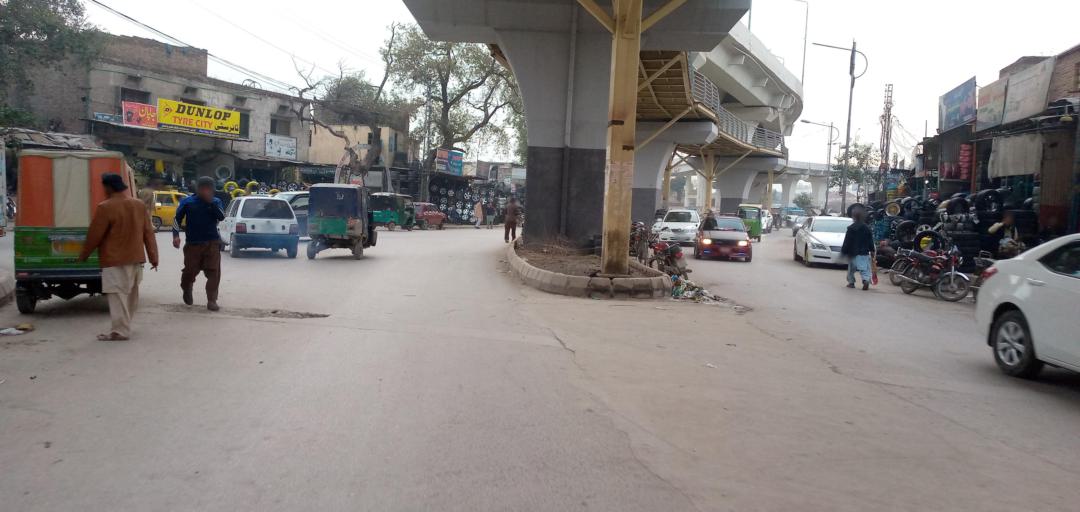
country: PK
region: Khyber Pakhtunkhwa
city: Peshawar
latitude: 34.0039
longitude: 71.5554
